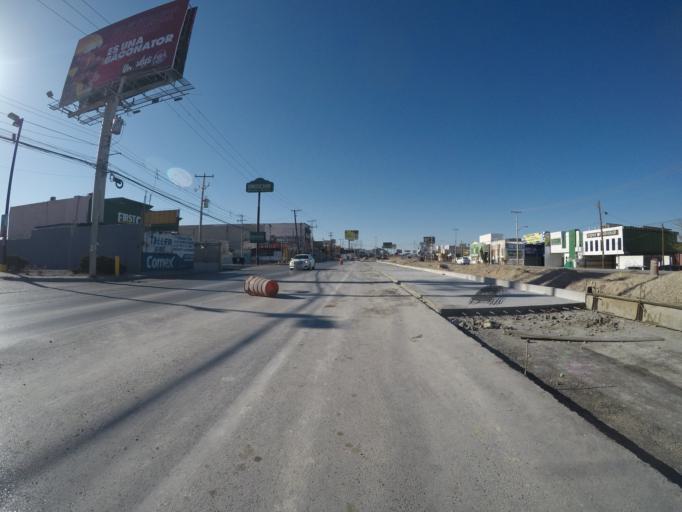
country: MX
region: Chihuahua
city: Ciudad Juarez
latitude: 31.6756
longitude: -106.4245
